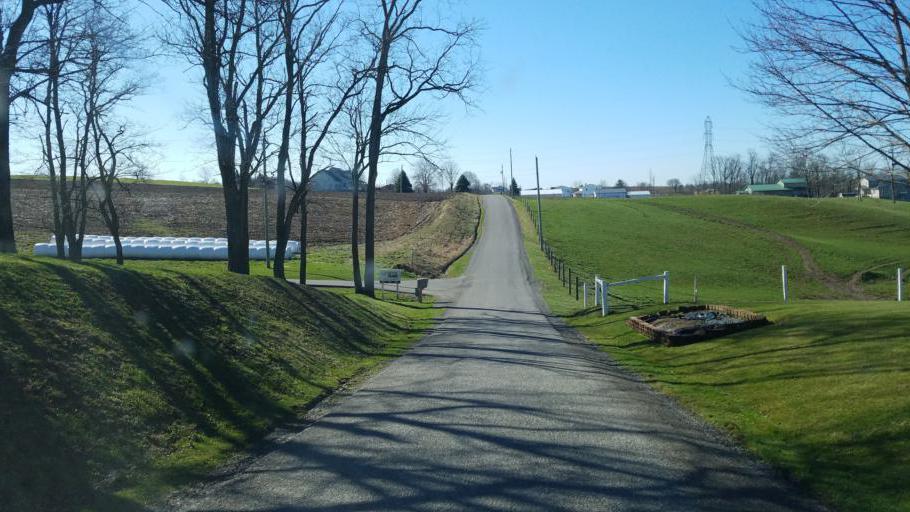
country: US
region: Ohio
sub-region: Wayne County
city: Apple Creek
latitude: 40.6288
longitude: -81.7991
